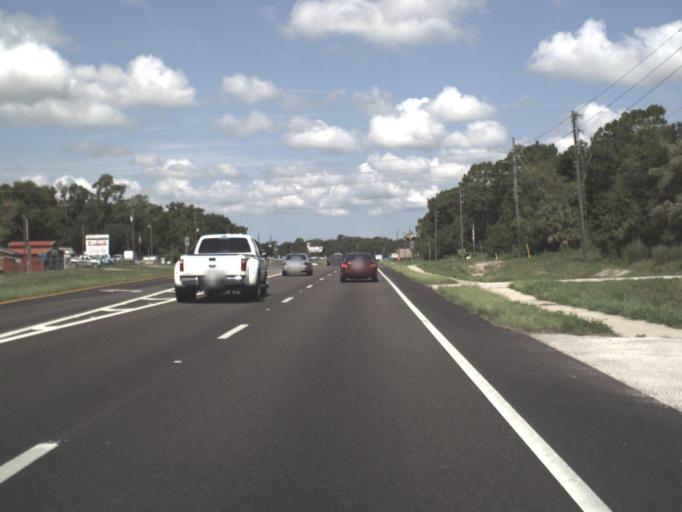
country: US
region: Florida
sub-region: Hernando County
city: Brookridge
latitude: 28.5410
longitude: -82.4577
